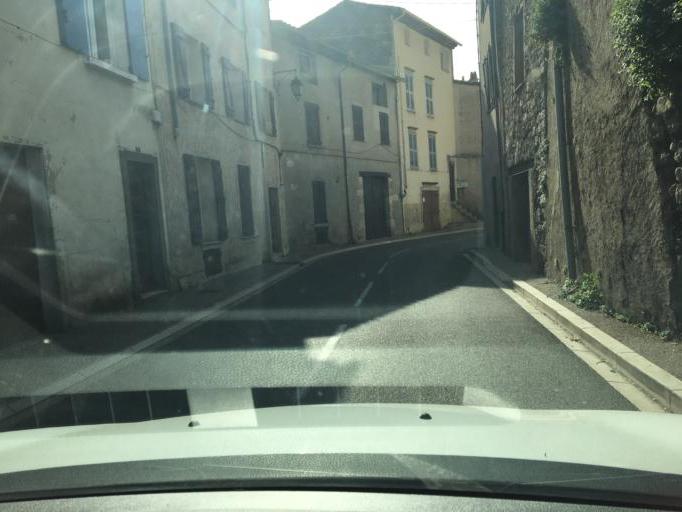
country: FR
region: Provence-Alpes-Cote d'Azur
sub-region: Departement du Var
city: Callas
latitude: 43.5924
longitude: 6.5392
